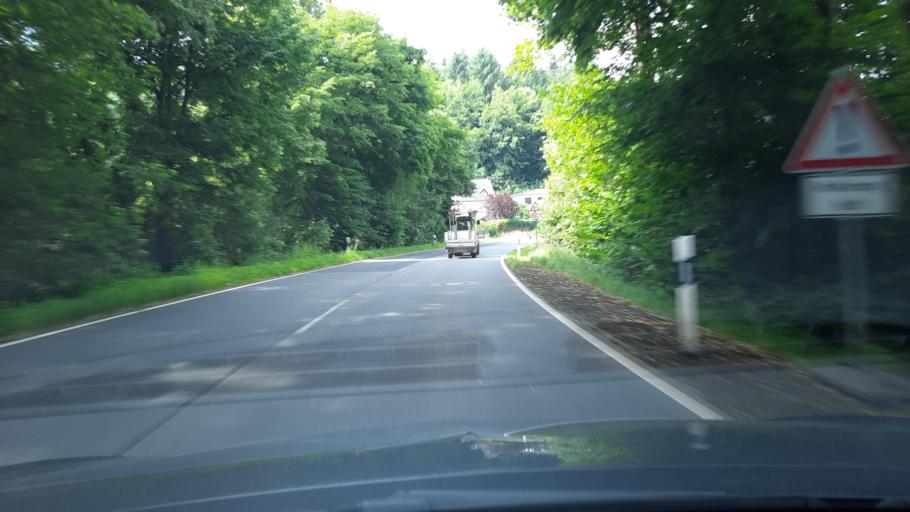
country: DE
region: Rheinland-Pfalz
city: Kempenich
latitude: 50.4186
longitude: 7.1230
